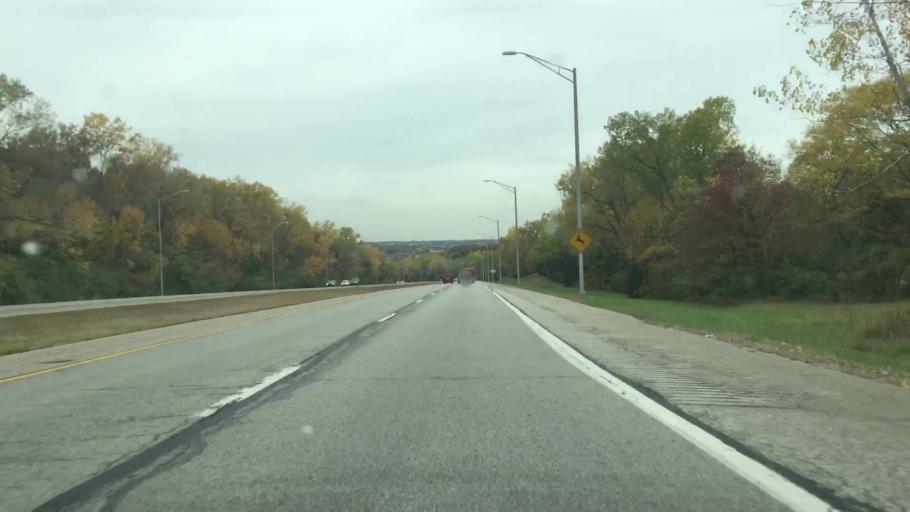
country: US
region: Kansas
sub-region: Wyandotte County
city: Edwardsville
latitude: 39.0107
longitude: -94.7933
